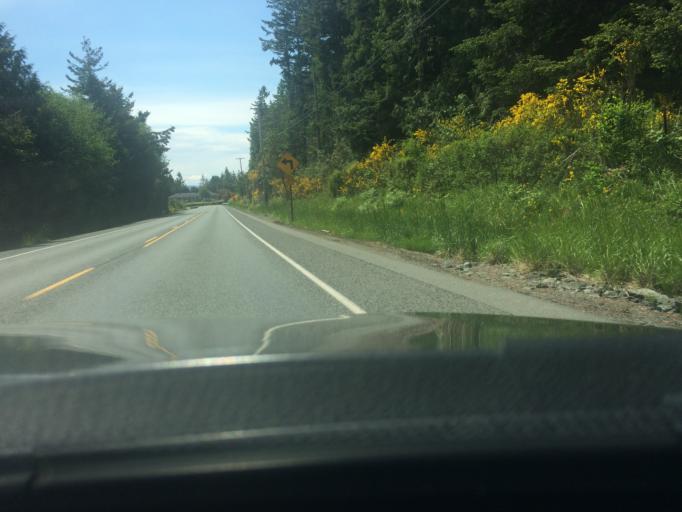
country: US
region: Washington
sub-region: Island County
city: Ault Field
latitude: 48.4259
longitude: -122.6649
